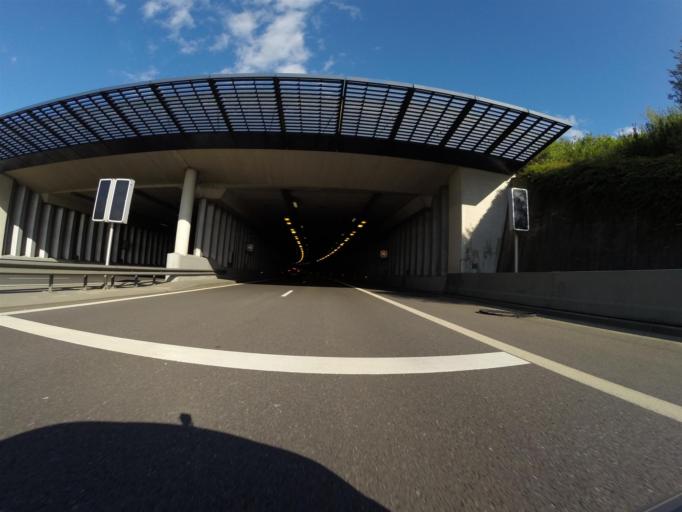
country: LU
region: Luxembourg
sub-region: Canton d'Esch-sur-Alzette
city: Frisange
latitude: 49.5070
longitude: 6.1902
